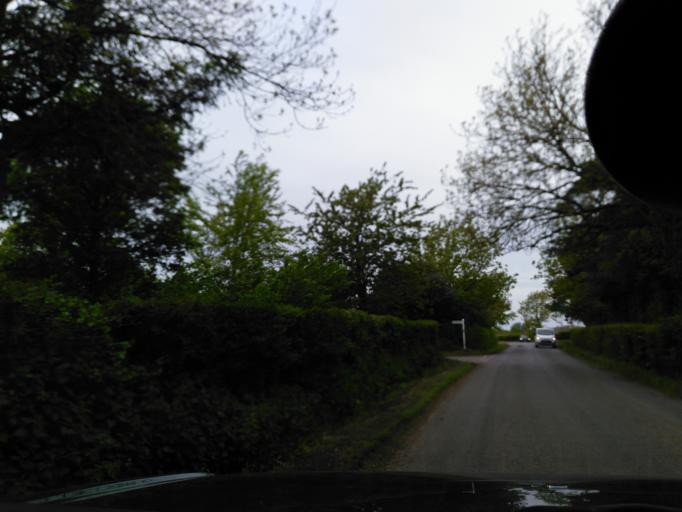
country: GB
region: England
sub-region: Wiltshire
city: Lacock
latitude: 51.4271
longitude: -2.1524
